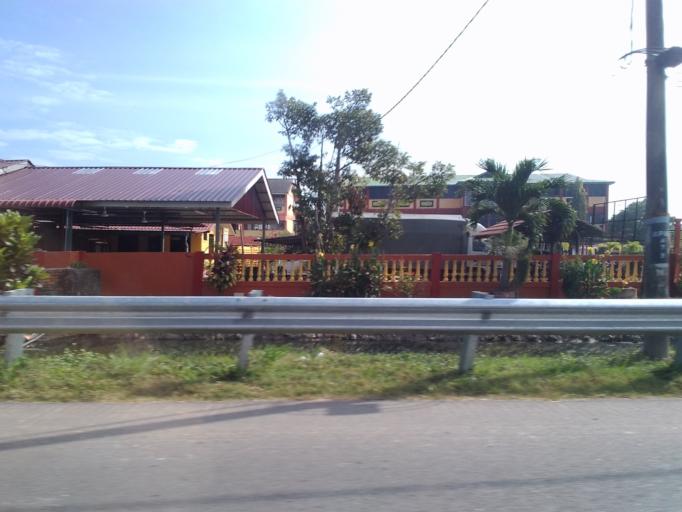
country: MY
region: Kedah
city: Gurun
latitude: 5.9522
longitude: 100.4082
